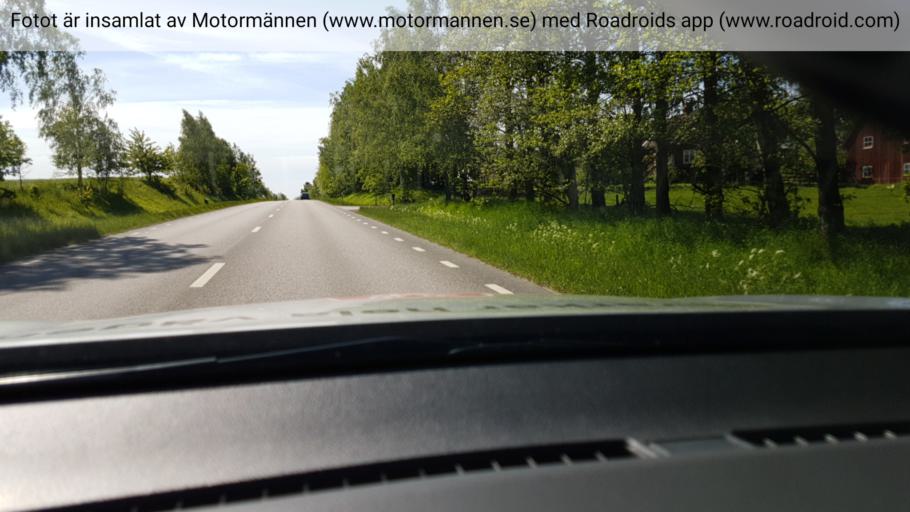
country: SE
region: Vaestra Goetaland
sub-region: Hjo Kommun
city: Hjo
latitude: 58.3288
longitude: 14.2570
